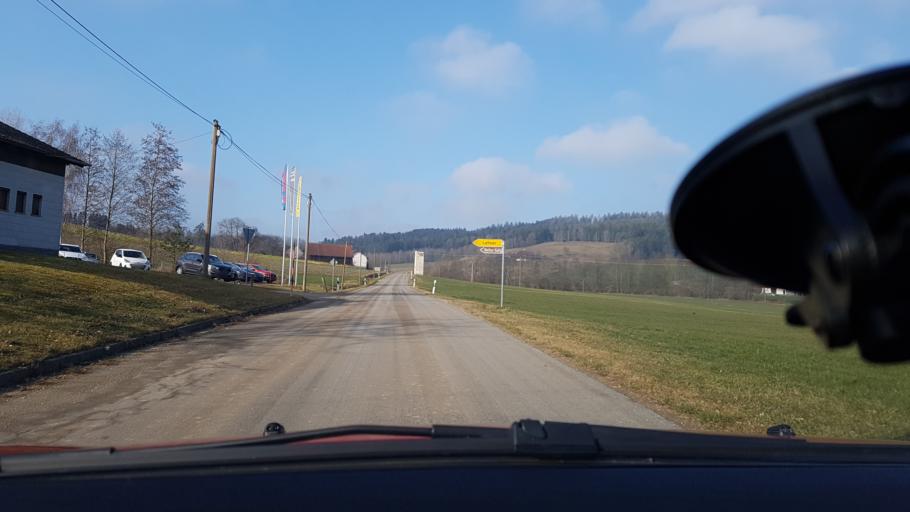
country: DE
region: Bavaria
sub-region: Lower Bavaria
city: Stubenberg
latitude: 48.3114
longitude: 13.0626
